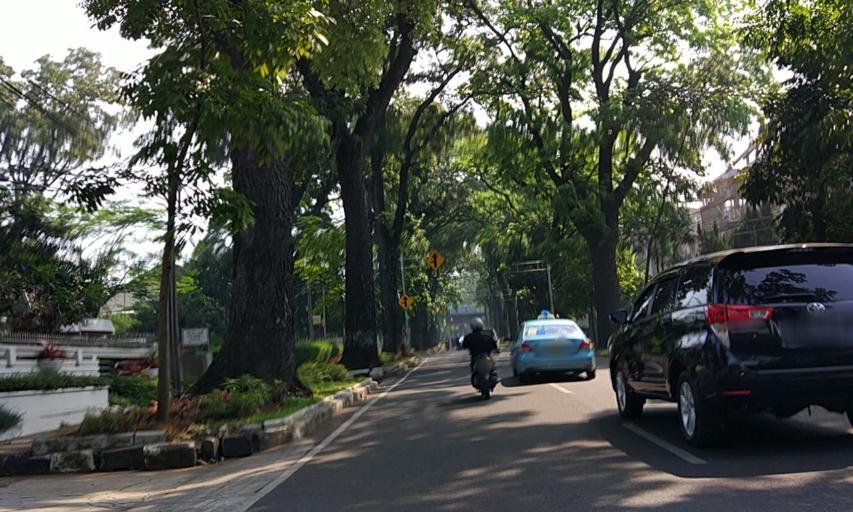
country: ID
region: West Java
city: Bandung
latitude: -6.9023
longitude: 107.6024
